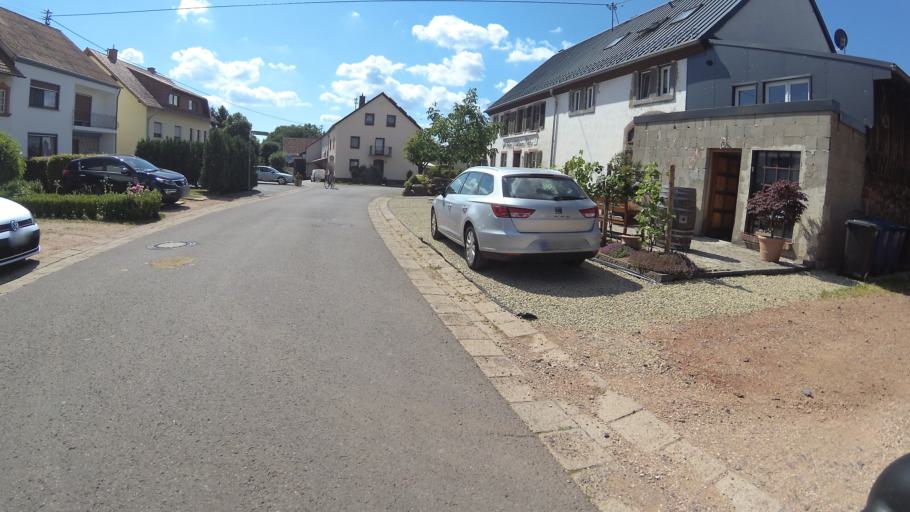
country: DE
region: Saarland
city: Weiskirchen
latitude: 49.5263
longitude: 6.8201
